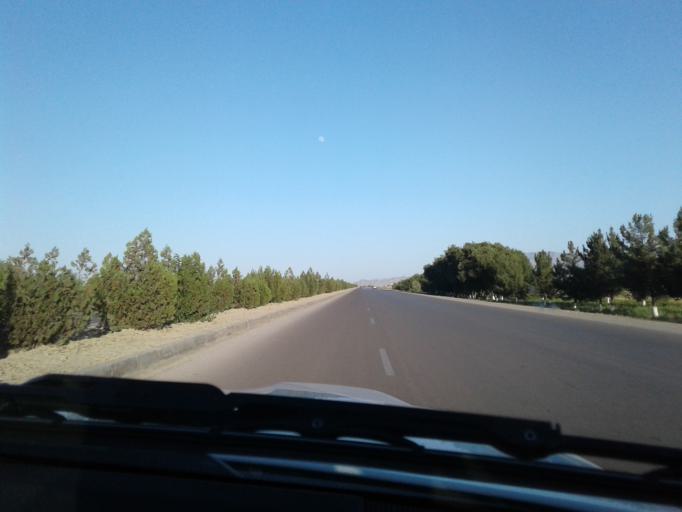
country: TM
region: Ahal
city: Baharly
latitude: 38.3402
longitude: 57.5646
